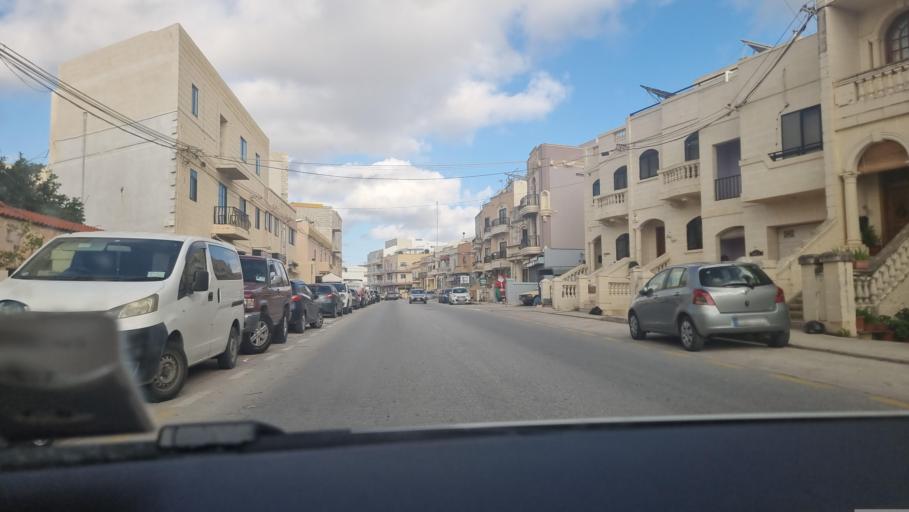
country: MT
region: Haz-Zebbug
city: Haz-Zebbug
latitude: 35.8764
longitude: 14.4371
